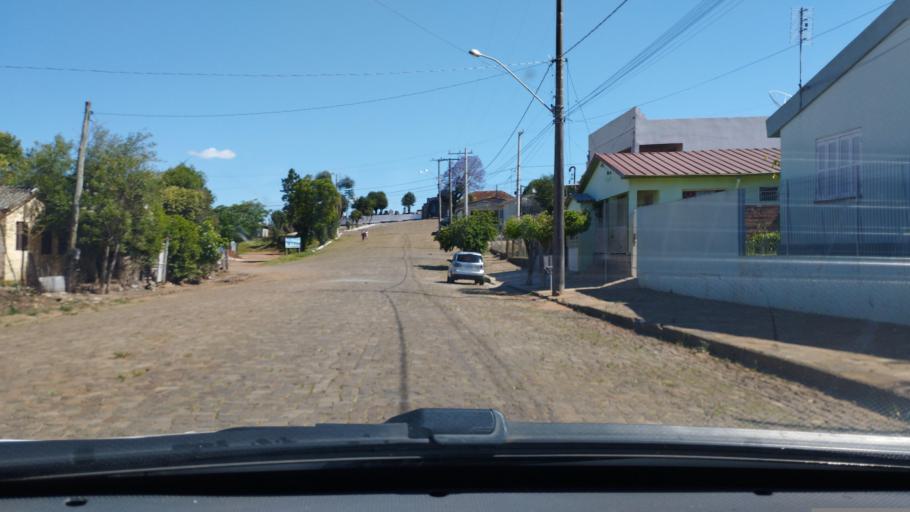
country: BR
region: Rio Grande do Sul
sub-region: Tupancireta
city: Tupancireta
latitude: -29.0898
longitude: -53.8346
